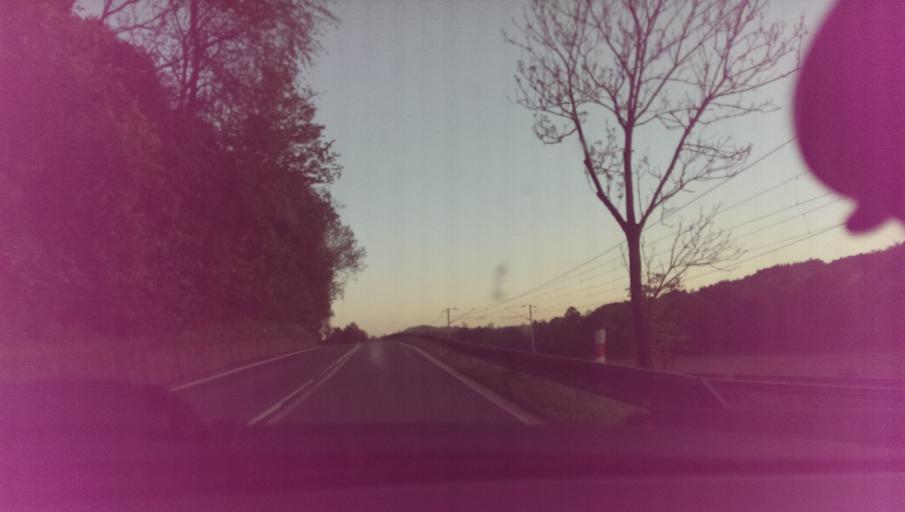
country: CZ
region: Zlin
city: Jablunka
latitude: 49.4052
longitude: 17.9538
